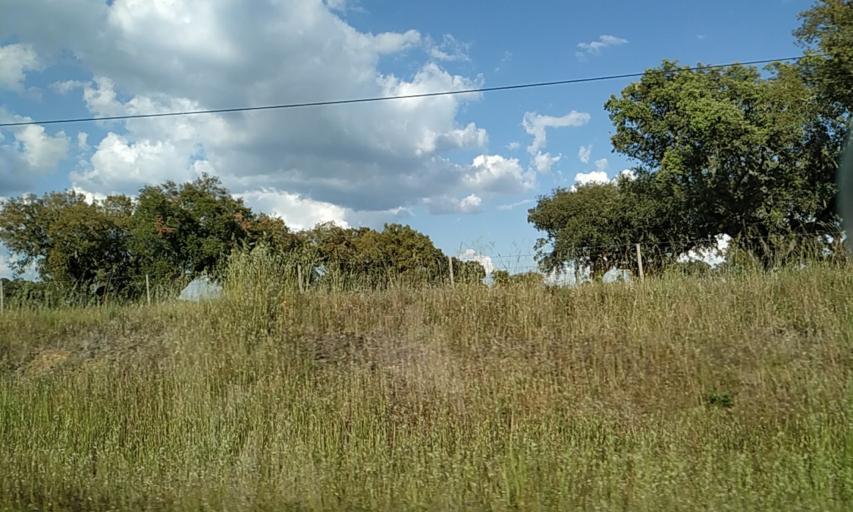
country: PT
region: Portalegre
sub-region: Portalegre
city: Urra
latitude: 39.1735
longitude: -7.4537
